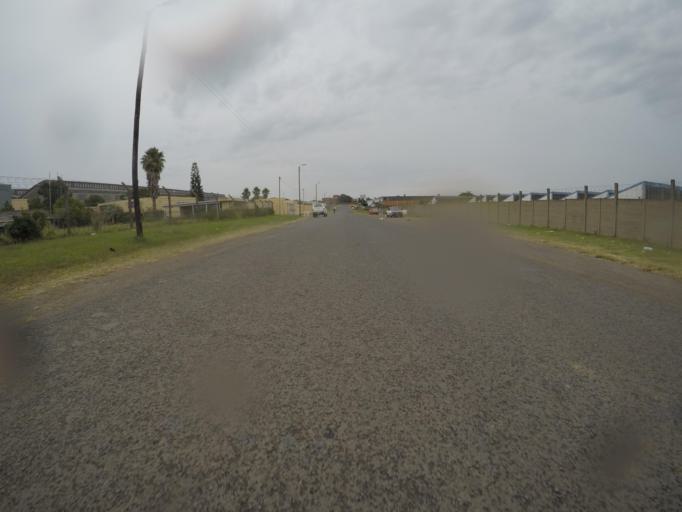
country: ZA
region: Eastern Cape
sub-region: Buffalo City Metropolitan Municipality
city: East London
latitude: -32.9754
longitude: 27.8226
